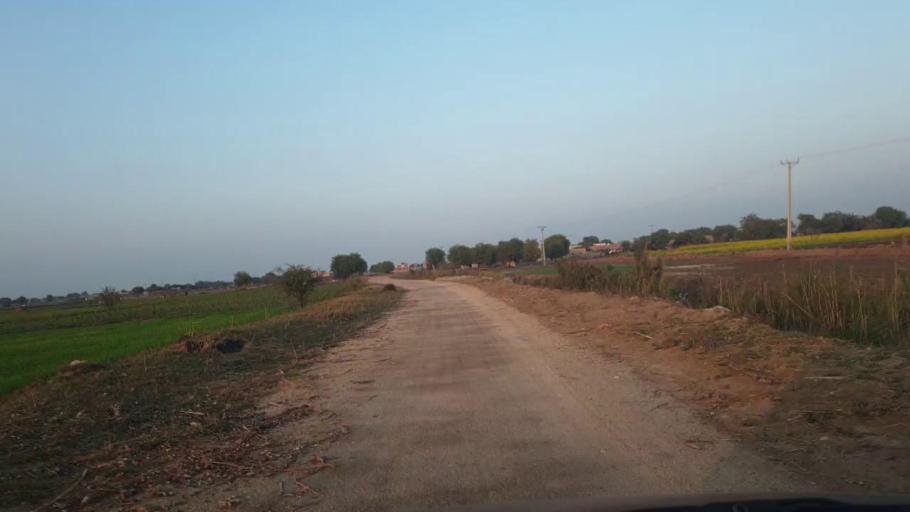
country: PK
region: Sindh
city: Berani
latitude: 25.8277
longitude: 68.7467
